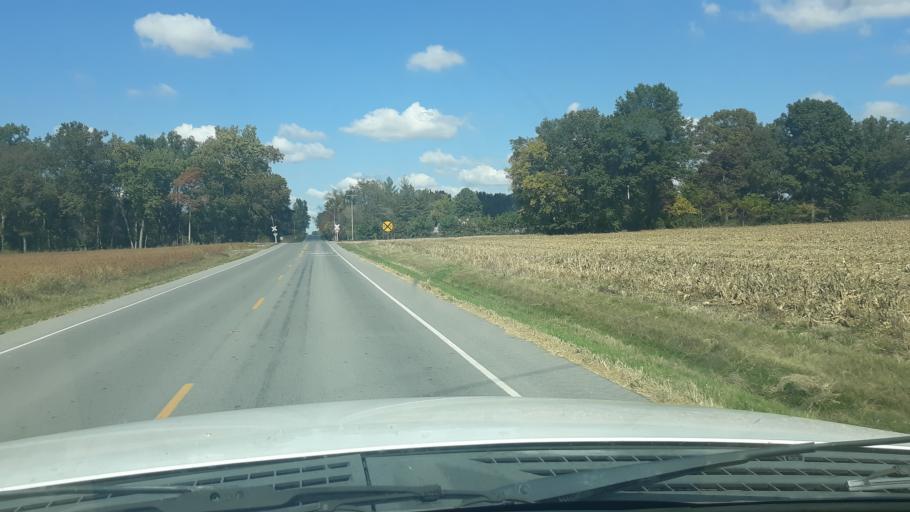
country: US
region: Illinois
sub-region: Saline County
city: Eldorado
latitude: 37.8107
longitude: -88.4848
